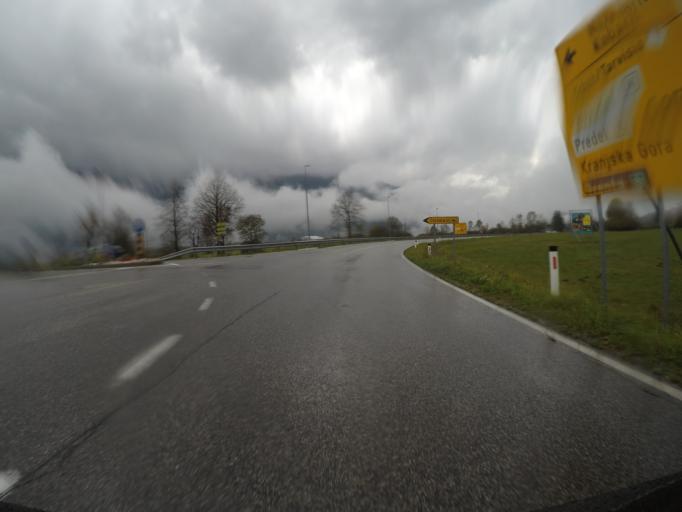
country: SI
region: Bovec
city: Bovec
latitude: 46.3339
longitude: 13.5570
